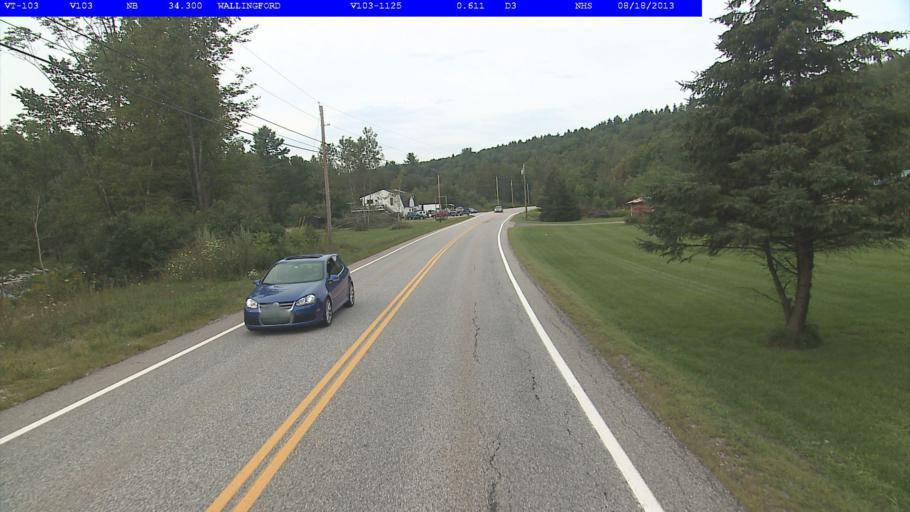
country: US
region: Vermont
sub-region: Rutland County
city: Rutland
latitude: 43.4555
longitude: -72.8785
